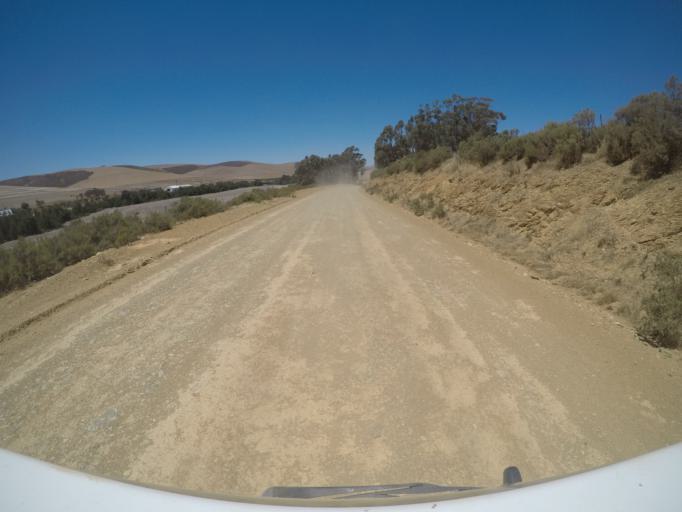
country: ZA
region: Western Cape
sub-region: Overberg District Municipality
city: Grabouw
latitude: -34.0980
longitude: 19.2006
